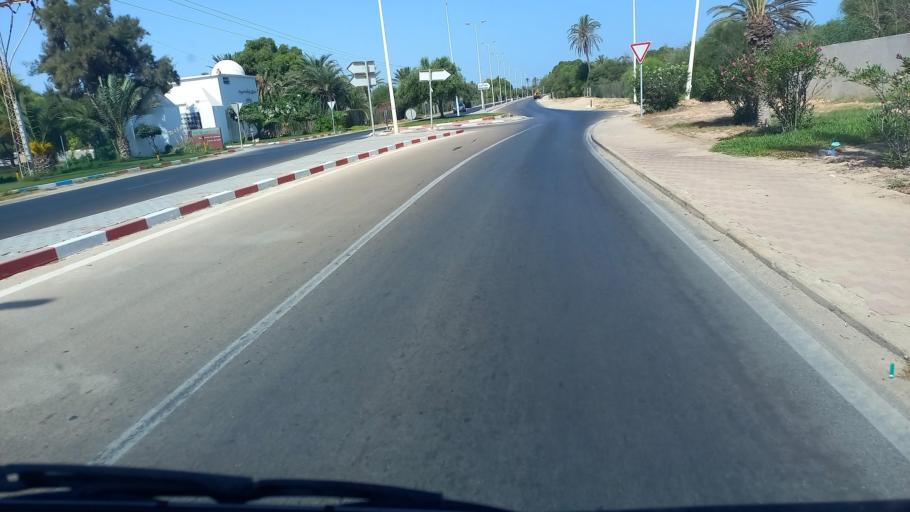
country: TN
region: Madanin
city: Midoun
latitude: 33.8274
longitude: 11.0131
